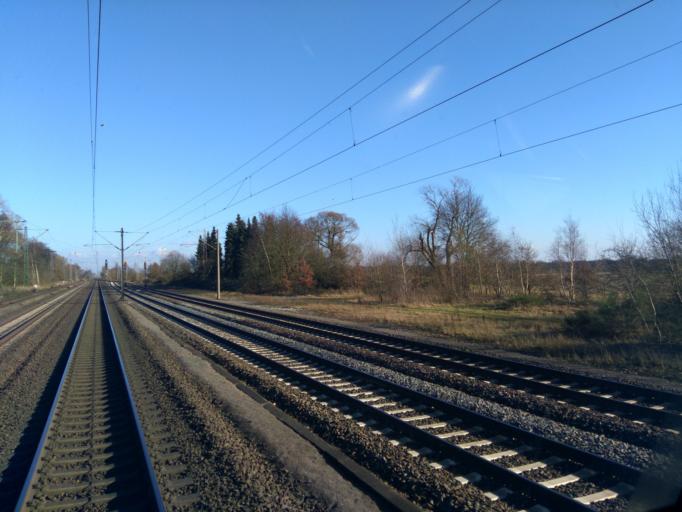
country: DE
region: Lower Saxony
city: Oyten
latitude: 53.0854
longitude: 9.0311
